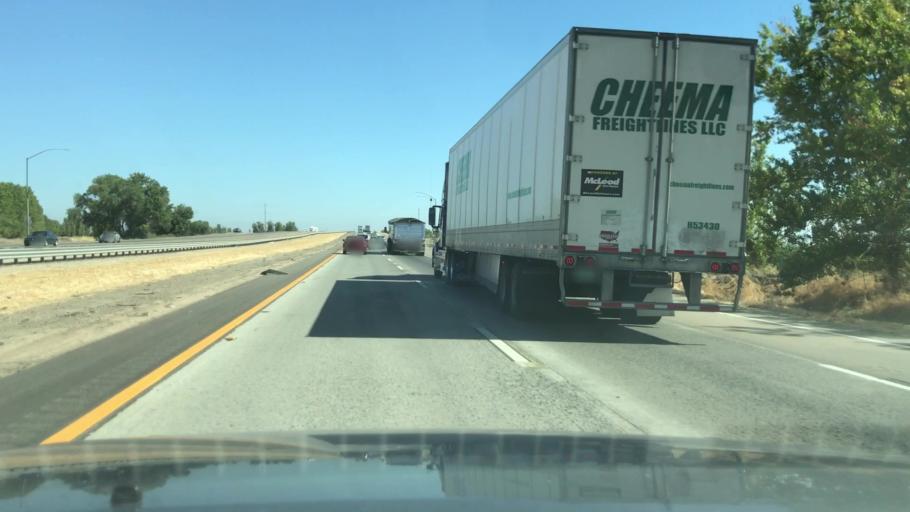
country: US
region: California
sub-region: San Joaquin County
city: Thornton
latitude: 38.1941
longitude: -121.4083
